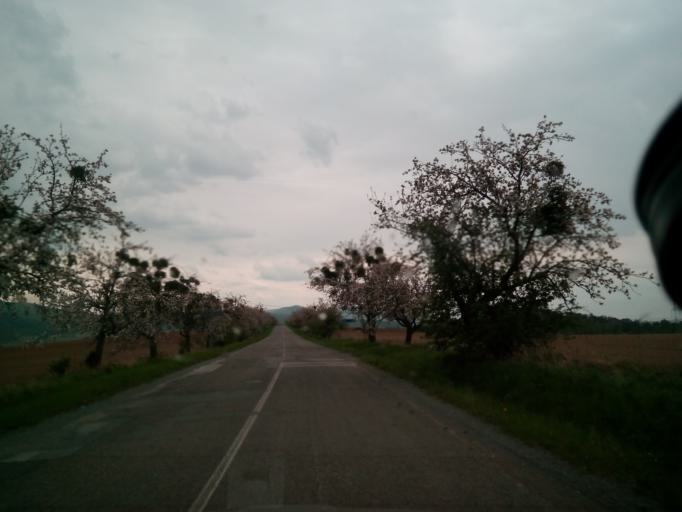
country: SK
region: Kosicky
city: Secovce
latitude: 48.7611
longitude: 21.4654
